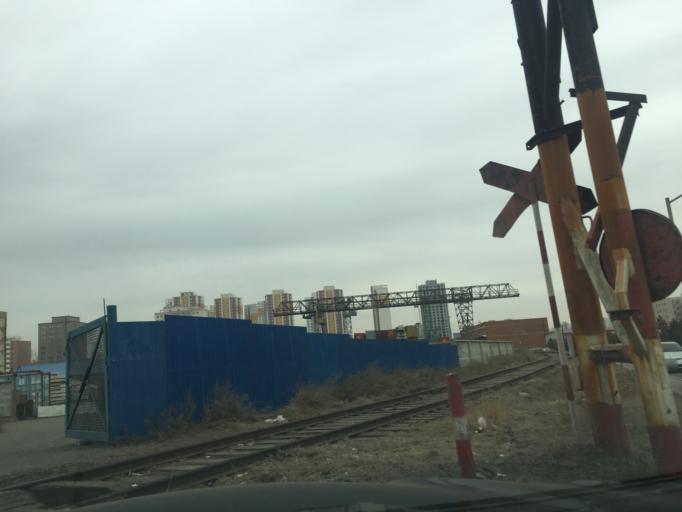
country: MN
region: Ulaanbaatar
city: Ulaanbaatar
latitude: 47.9048
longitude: 106.8878
